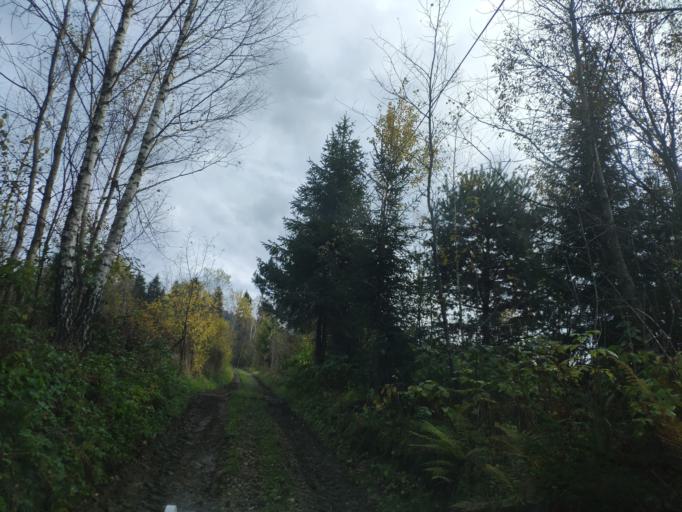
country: SK
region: Kosicky
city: Spisska Nova Ves
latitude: 48.8237
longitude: 20.6224
